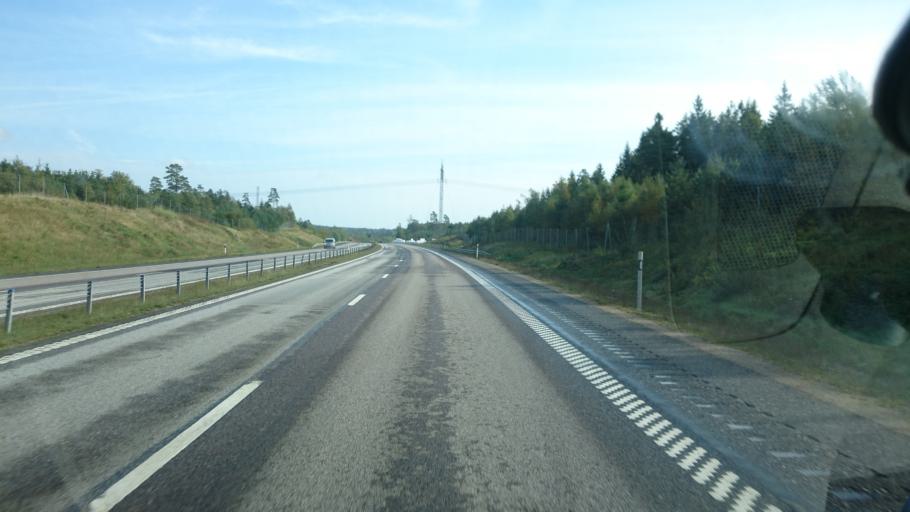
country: SE
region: Vaestra Goetaland
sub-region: Uddevalla Kommun
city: Uddevalla
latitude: 58.3316
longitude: 12.0970
